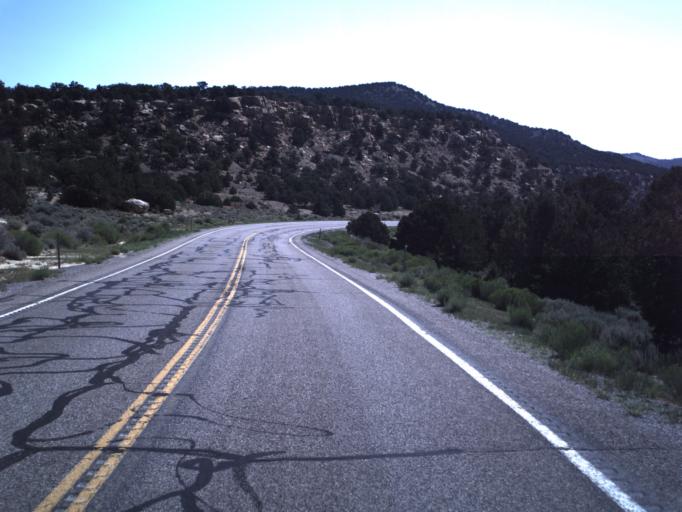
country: US
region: Utah
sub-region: Wayne County
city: Loa
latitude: 38.6723
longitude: -111.4114
